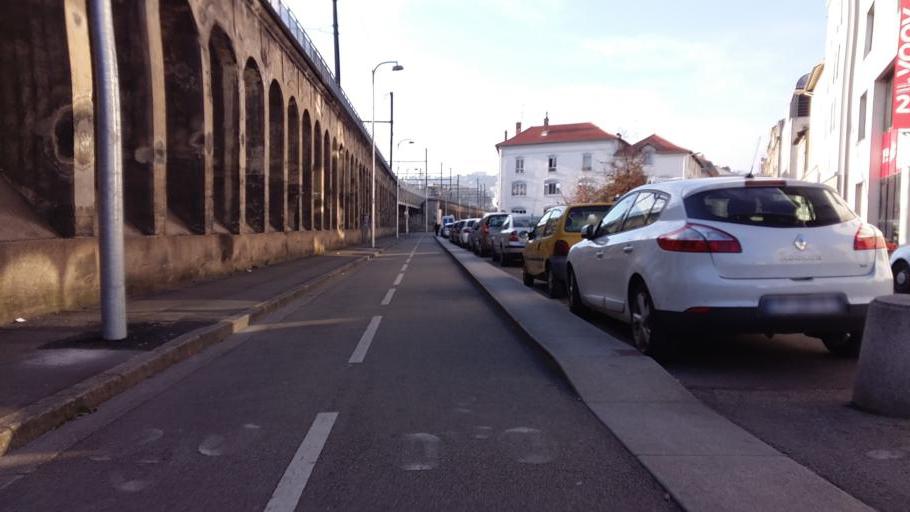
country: FR
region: Rhone-Alpes
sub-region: Departement du Rhone
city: Lyon
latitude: 45.7456
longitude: 4.8379
